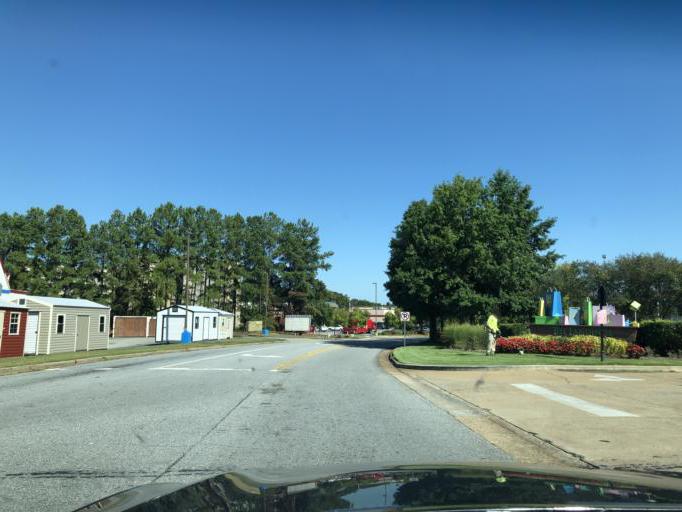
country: US
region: Alabama
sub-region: Russell County
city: Phenix City
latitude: 32.5182
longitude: -84.9559
